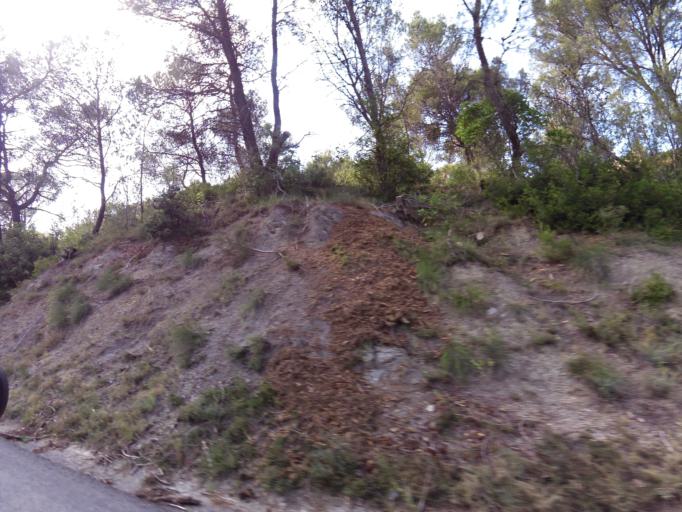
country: FR
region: Languedoc-Roussillon
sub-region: Departement du Gard
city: Quissac
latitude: 43.8423
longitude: 4.0262
